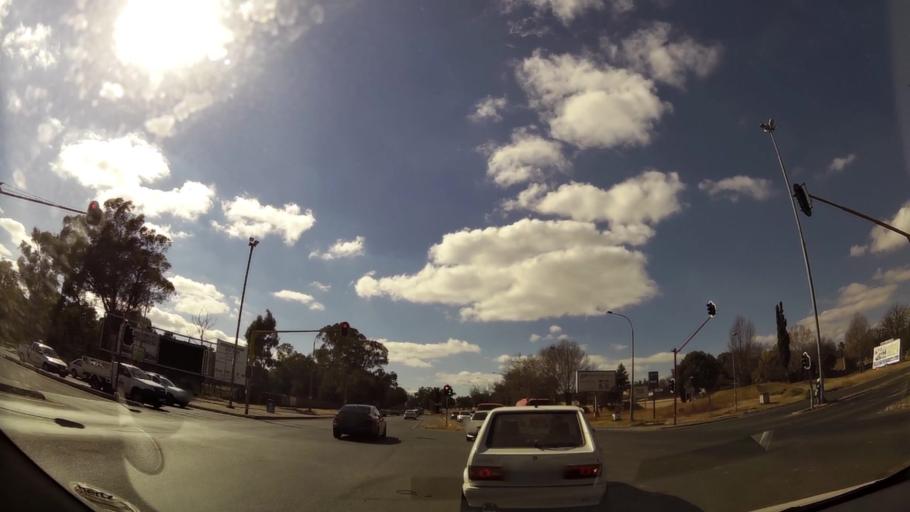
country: ZA
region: Gauteng
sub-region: West Rand District Municipality
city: Krugersdorp
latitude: -26.0878
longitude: 27.7847
